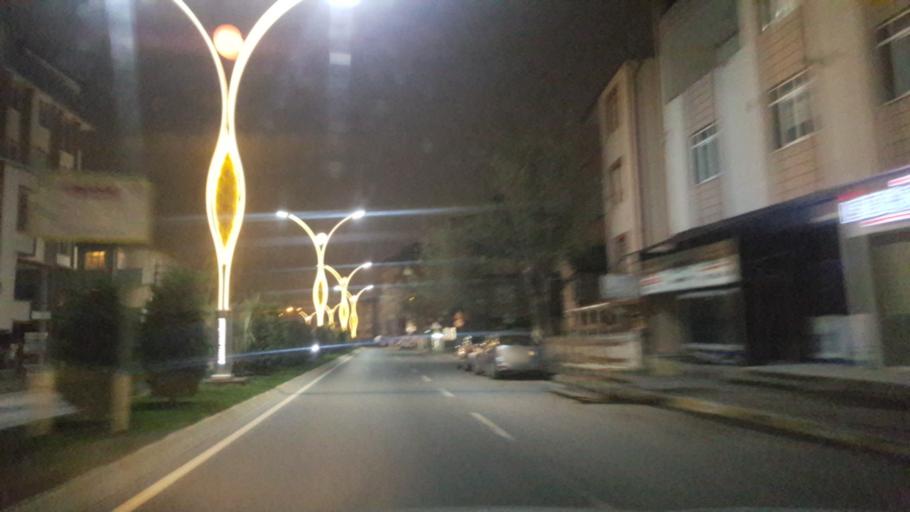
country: TR
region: Kocaeli
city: Darica
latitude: 40.7813
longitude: 29.3979
